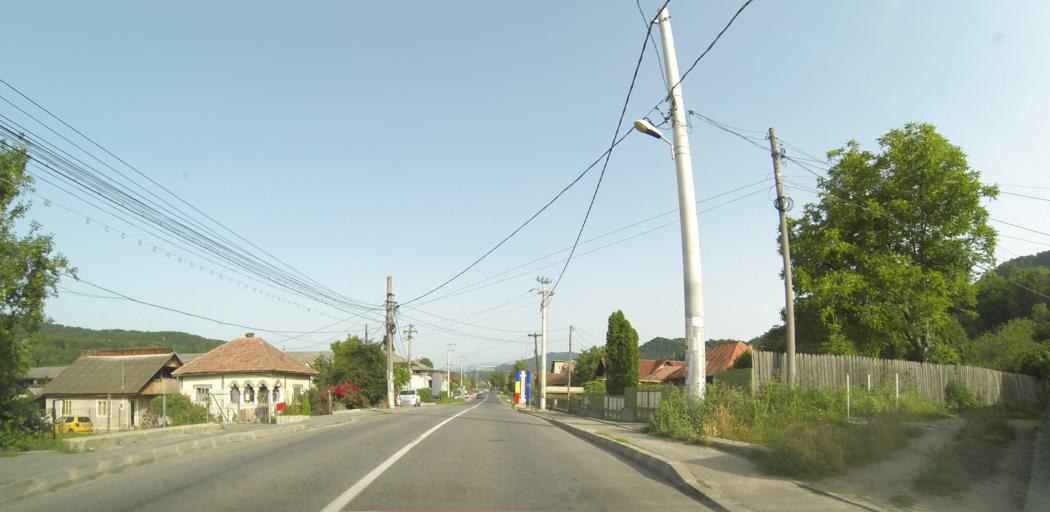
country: RO
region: Valcea
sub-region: Comuna Vladesti
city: Vladesti
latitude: 45.1136
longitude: 24.3219
